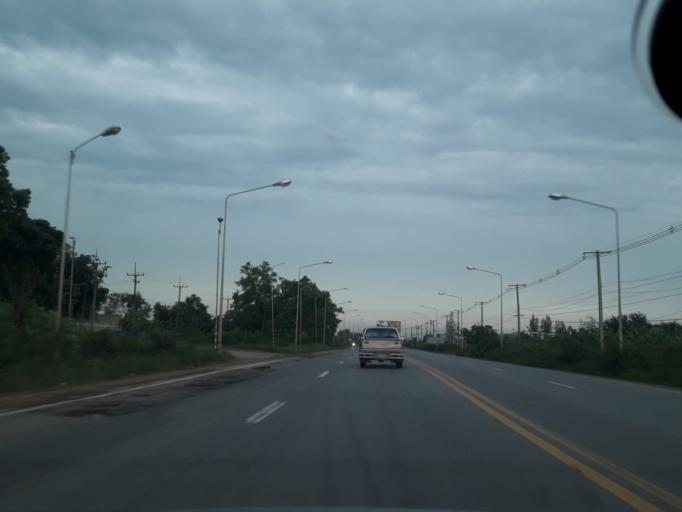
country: TH
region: Pathum Thani
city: Ban Rangsit
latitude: 14.0569
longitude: 100.7471
